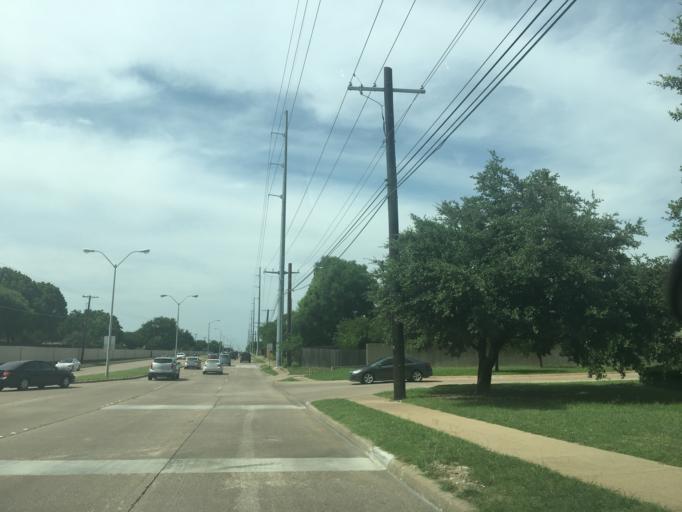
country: US
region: Texas
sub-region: Dallas County
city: Richardson
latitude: 32.9475
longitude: -96.6827
